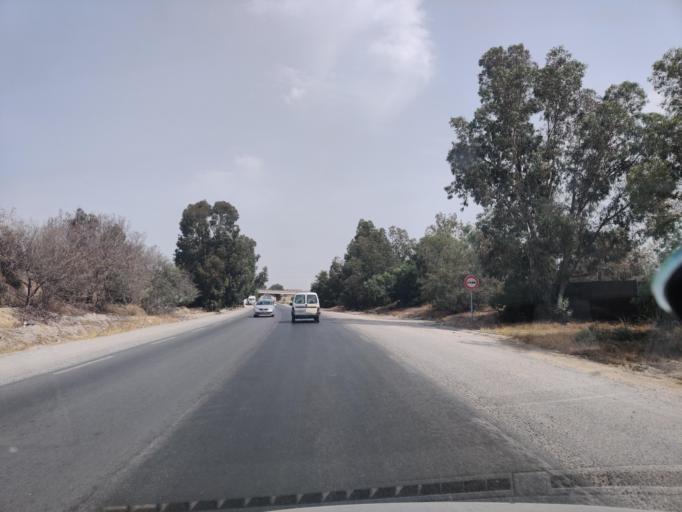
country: TN
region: Nabul
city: Al Hammamat
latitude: 36.4383
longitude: 10.5734
